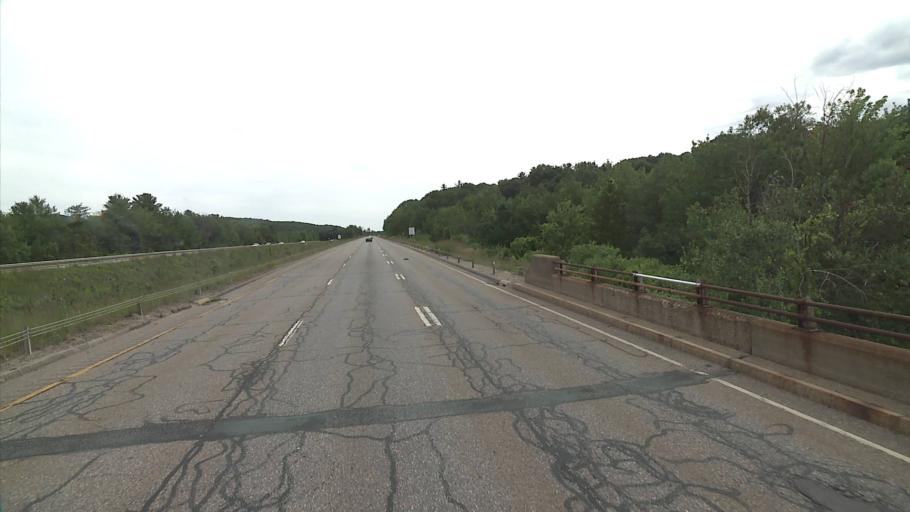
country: US
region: Connecticut
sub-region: Litchfield County
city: Torrington
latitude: 41.8212
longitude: -73.1110
